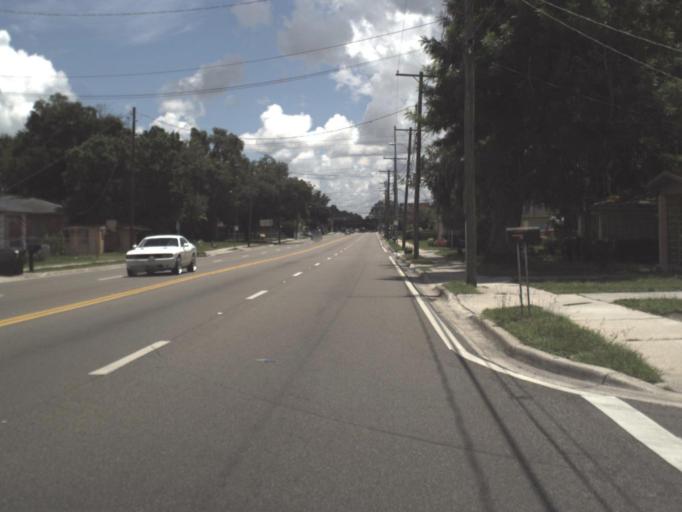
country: US
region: Florida
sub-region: Hillsborough County
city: East Lake-Orient Park
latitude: 27.9814
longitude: -82.4209
